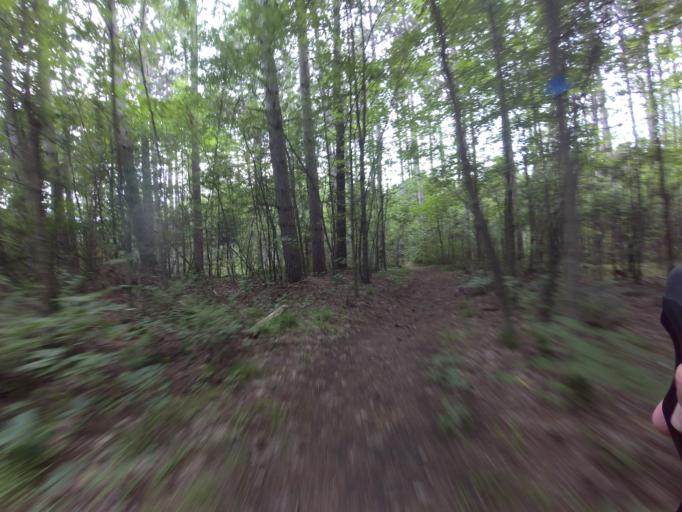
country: CA
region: Ontario
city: Bells Corners
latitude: 45.0311
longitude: -75.6604
